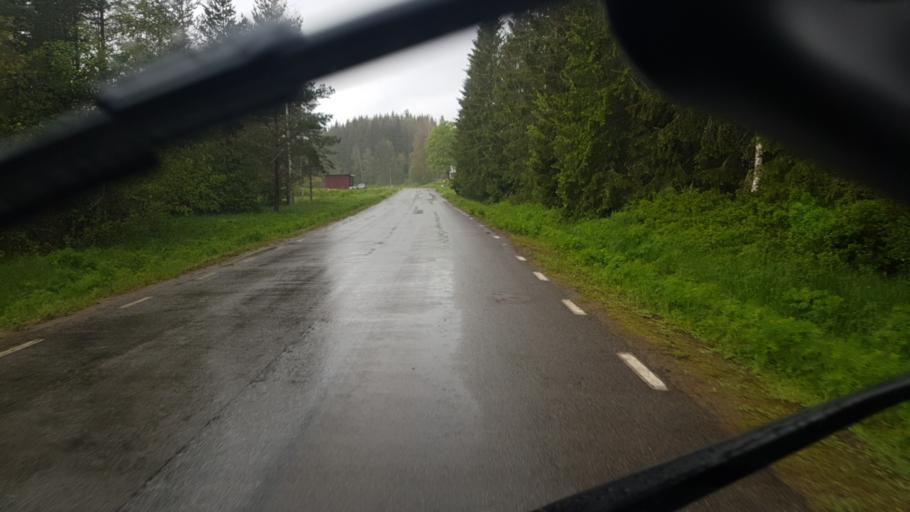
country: SE
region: Vaermland
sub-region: Eda Kommun
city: Amotfors
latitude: 59.7011
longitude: 12.4564
